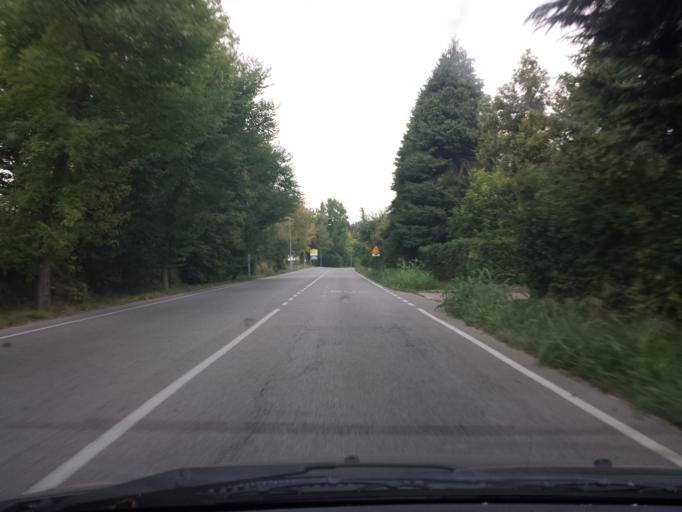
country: IT
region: Veneto
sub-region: Provincia di Vicenza
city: Monticello Conte Otto
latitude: 45.5806
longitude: 11.5529
